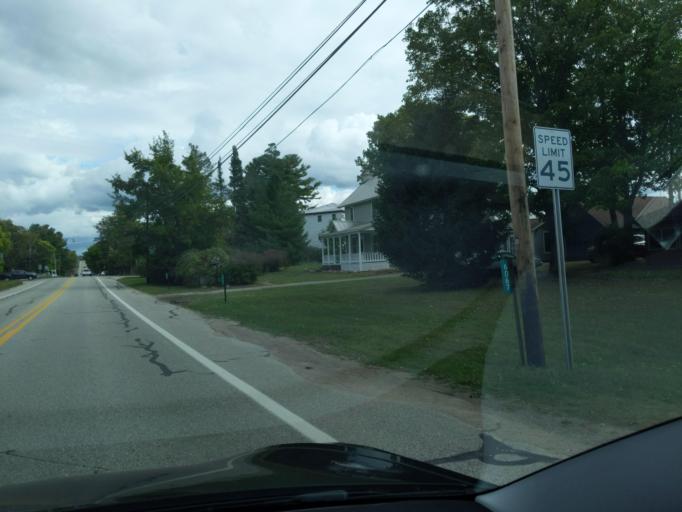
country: US
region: Michigan
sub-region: Antrim County
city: Bellaire
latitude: 45.1071
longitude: -85.3515
